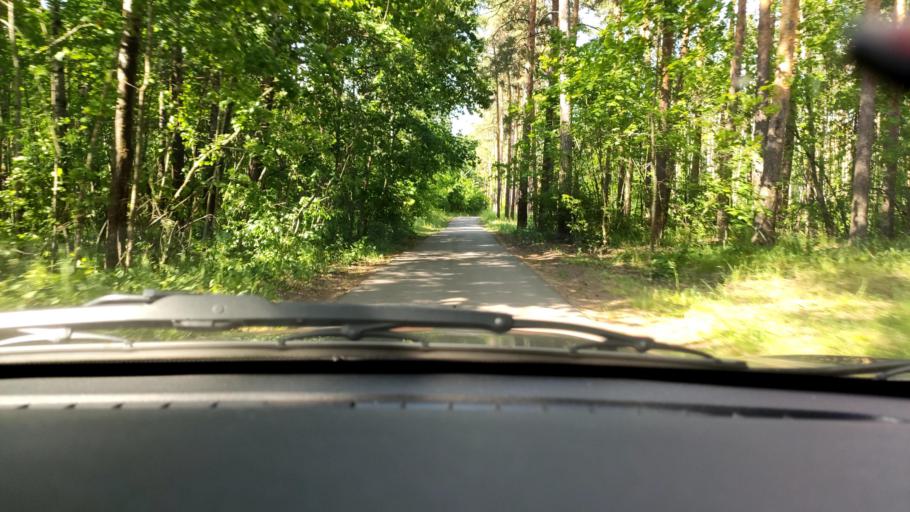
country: RU
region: Voronezj
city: Somovo
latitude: 51.8060
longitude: 39.3821
